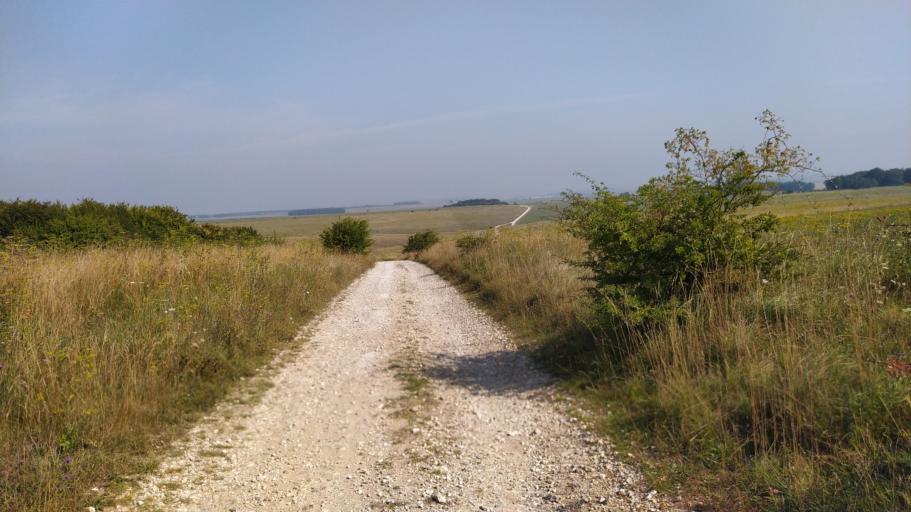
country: GB
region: England
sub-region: Wiltshire
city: Shrewton
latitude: 51.1740
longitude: -1.9521
